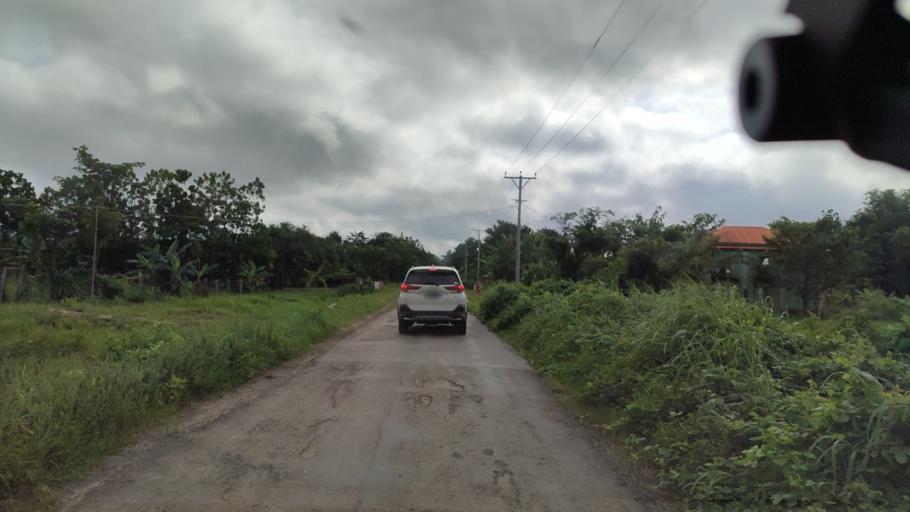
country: MM
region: Bago
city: Letpandan
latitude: 17.7971
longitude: 95.8540
